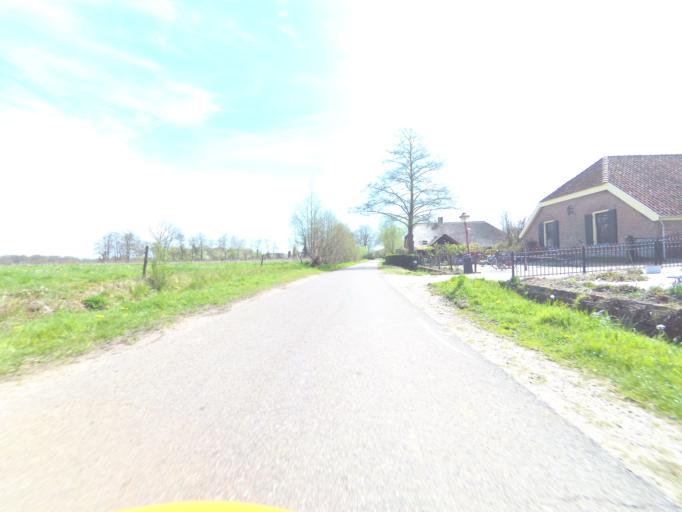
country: NL
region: Gelderland
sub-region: Gemeente Nijkerk
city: Nijkerk
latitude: 52.2413
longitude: 5.4999
